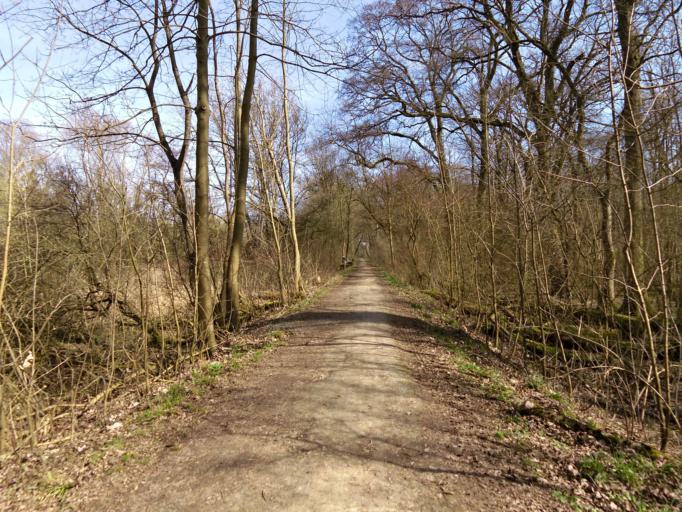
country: DE
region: Hesse
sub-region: Regierungsbezirk Darmstadt
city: Stockstadt am Rhein
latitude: 49.8305
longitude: 8.4520
